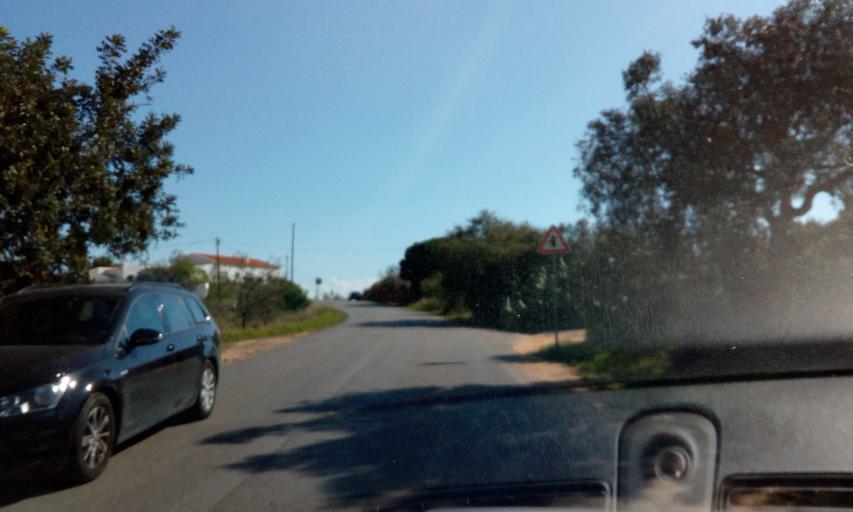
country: PT
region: Faro
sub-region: Albufeira
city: Ferreiras
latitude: 37.1127
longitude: -8.2125
